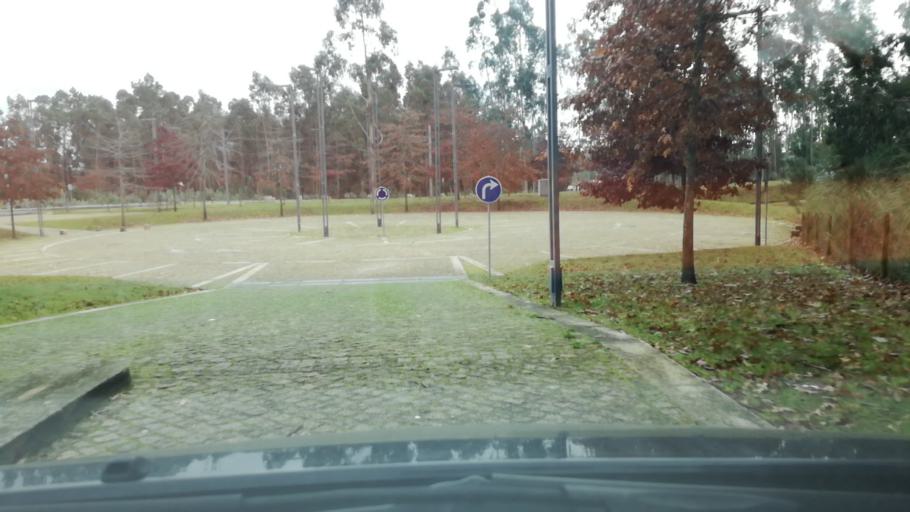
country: PT
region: Porto
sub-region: Maia
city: Anta
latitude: 41.2536
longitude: -8.6297
